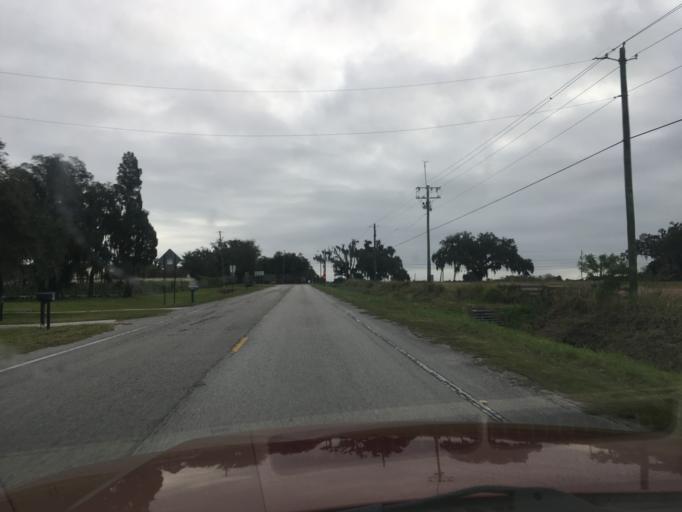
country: US
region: Florida
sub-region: Hillsborough County
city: Plant City
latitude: 28.0476
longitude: -82.0990
